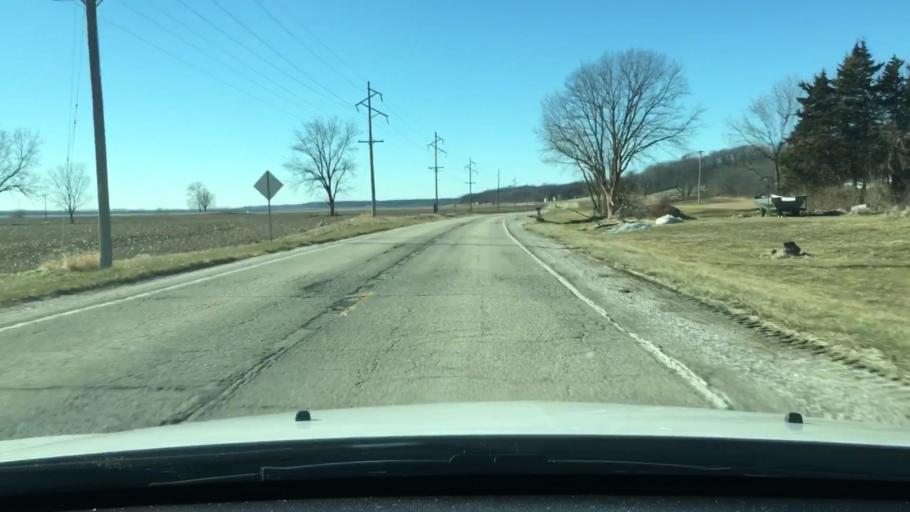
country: US
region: Illinois
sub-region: Fulton County
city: Astoria
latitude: 40.1796
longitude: -90.2333
